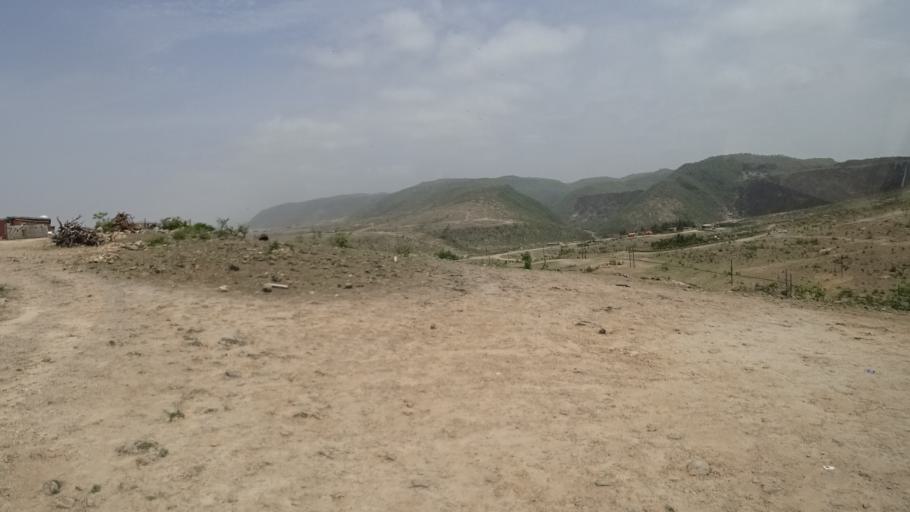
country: OM
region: Zufar
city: Salalah
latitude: 17.0665
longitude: 54.4360
